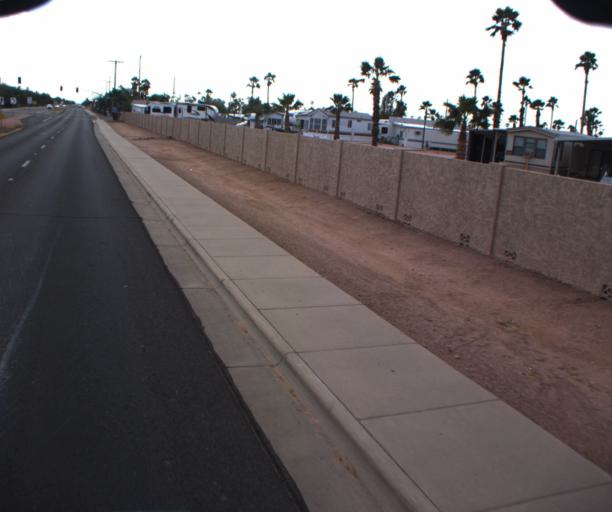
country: US
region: Arizona
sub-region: Pinal County
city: Apache Junction
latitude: 33.4091
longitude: -111.5462
